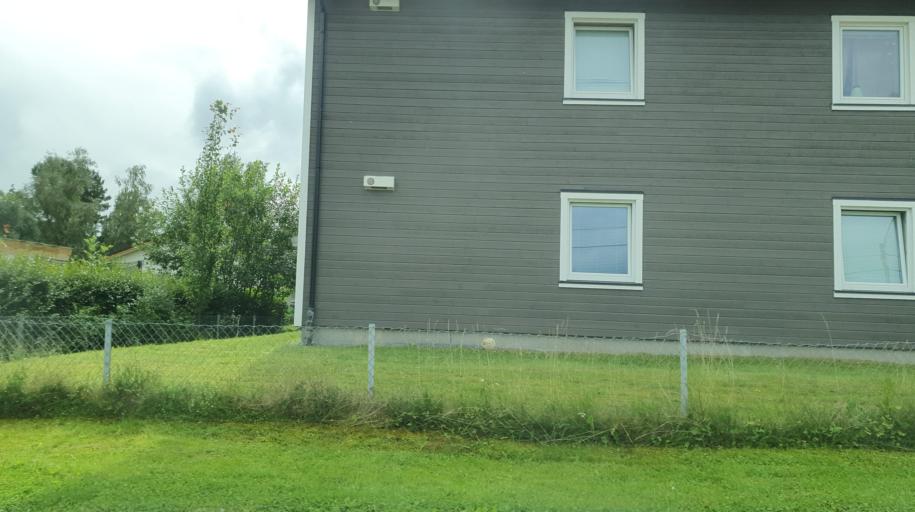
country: NO
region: Nord-Trondelag
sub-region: Stjordal
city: Stjordalshalsen
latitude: 63.4514
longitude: 10.9763
